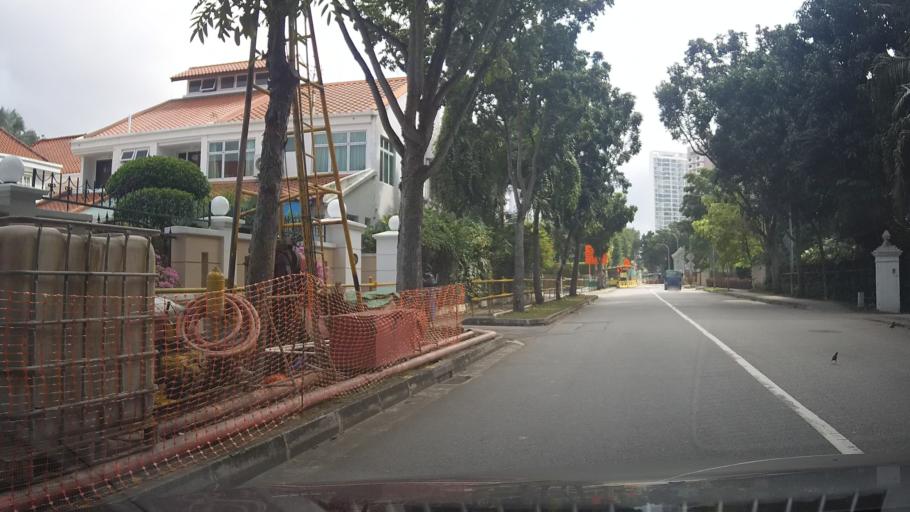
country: SG
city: Singapore
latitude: 1.2974
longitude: 103.8920
